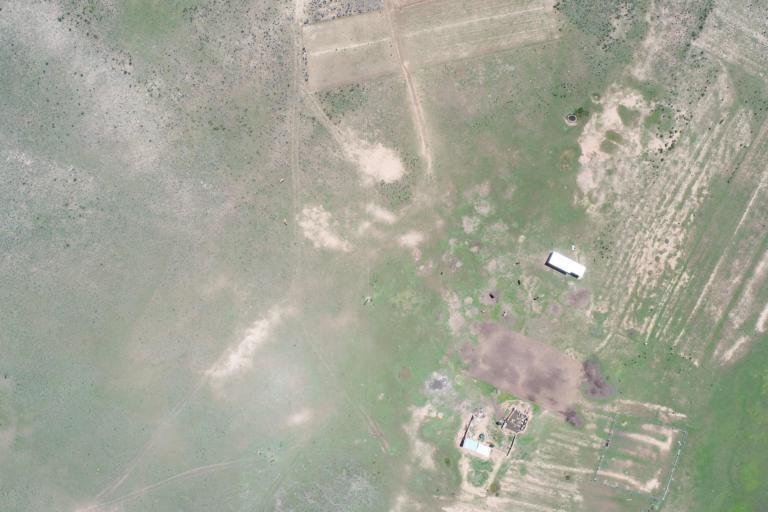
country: BO
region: La Paz
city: Curahuara de Carangas
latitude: -17.3125
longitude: -68.5151
